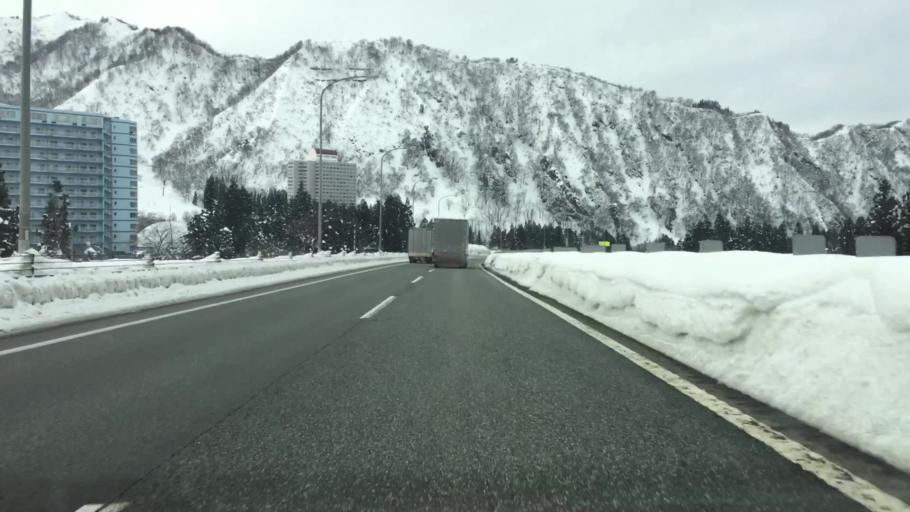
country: JP
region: Niigata
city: Shiozawa
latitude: 36.9070
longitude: 138.8442
